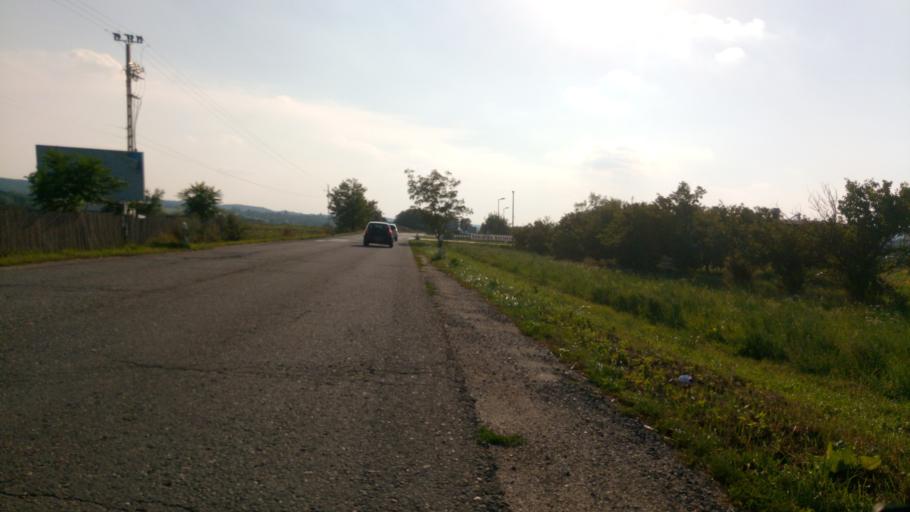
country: HU
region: Pest
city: Budaors
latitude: 47.4454
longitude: 18.9510
